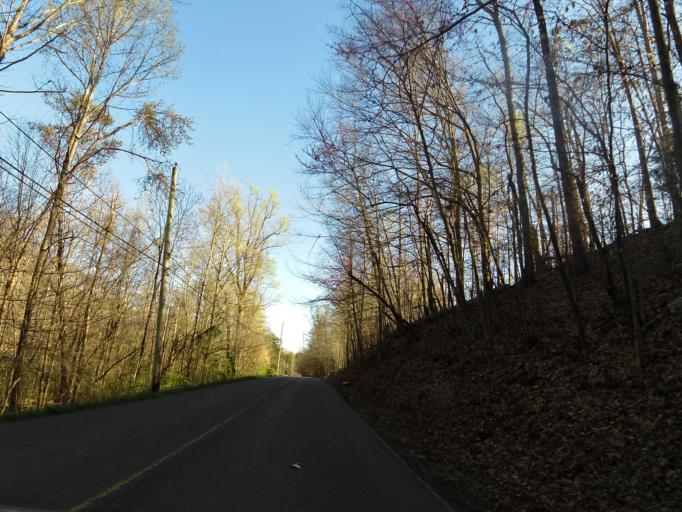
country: US
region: Tennessee
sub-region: Knox County
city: Mascot
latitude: 36.0006
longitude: -83.7659
